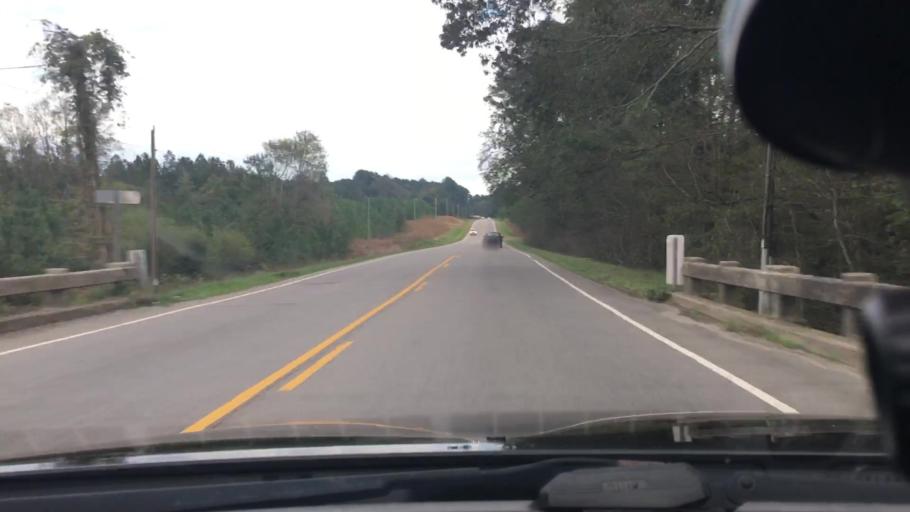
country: US
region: North Carolina
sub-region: Moore County
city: Carthage
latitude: 35.3829
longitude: -79.4852
